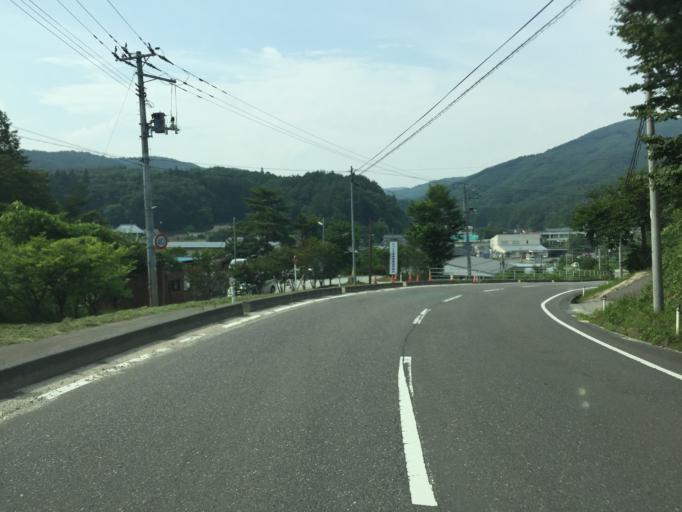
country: JP
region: Fukushima
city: Funehikimachi-funehiki
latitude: 37.4992
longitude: 140.7646
